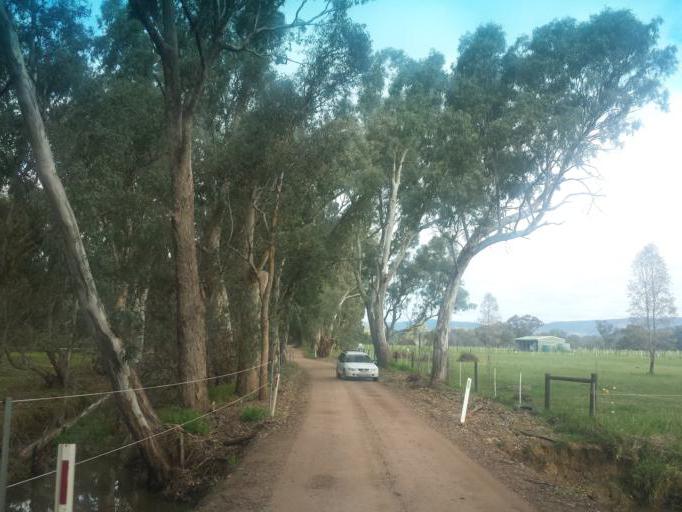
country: AU
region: Victoria
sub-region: Murrindindi
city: Kinglake West
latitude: -37.0327
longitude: 145.2318
